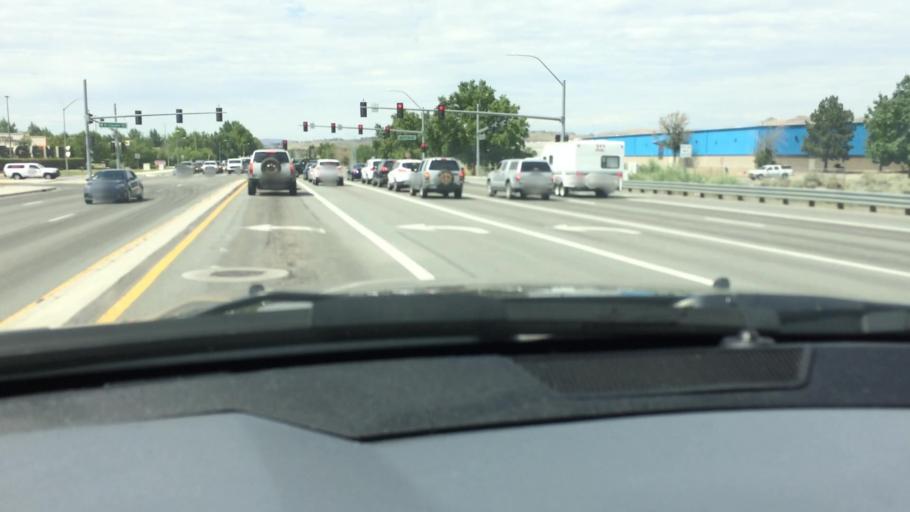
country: US
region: Nevada
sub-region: Washoe County
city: Sparks
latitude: 39.5328
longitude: -119.7154
